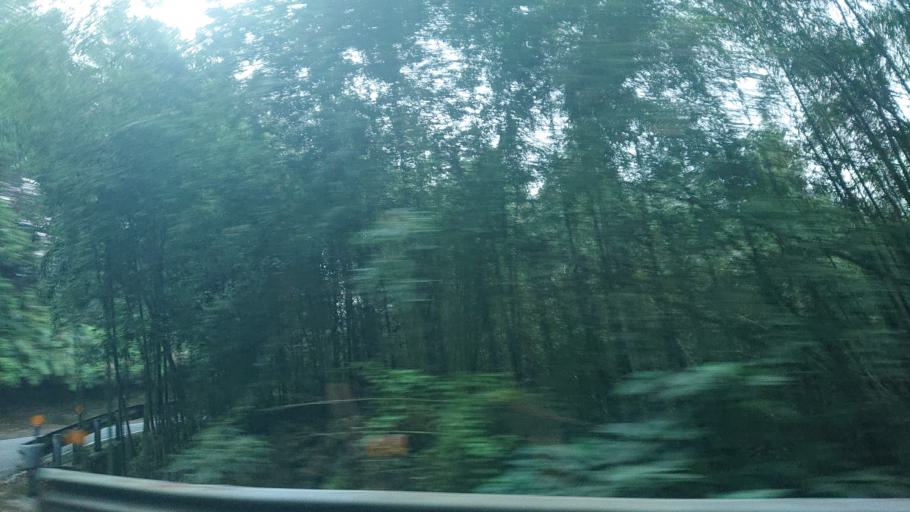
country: TW
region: Taiwan
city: Lugu
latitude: 23.5123
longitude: 120.7015
